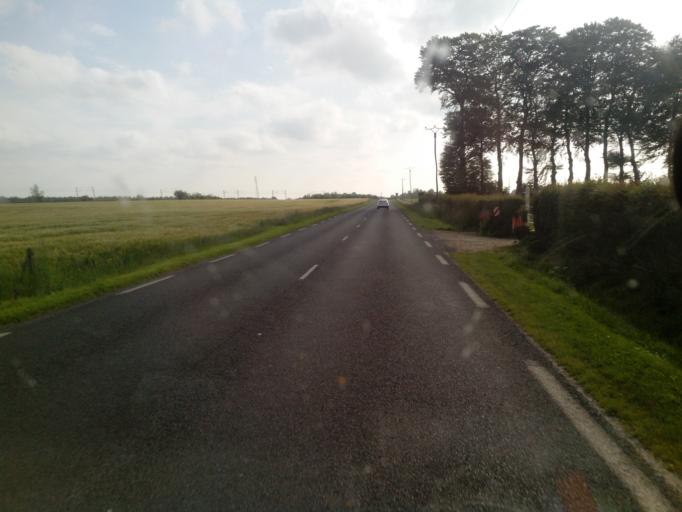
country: FR
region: Haute-Normandie
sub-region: Departement de la Seine-Maritime
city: Sainte-Marie-des-Champs
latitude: 49.6360
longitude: 0.8192
